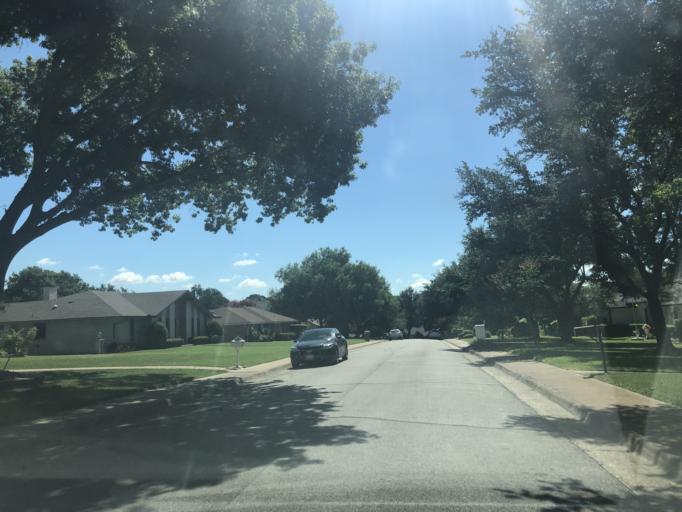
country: US
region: Texas
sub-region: Dallas County
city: Duncanville
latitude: 32.6377
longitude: -96.9284
